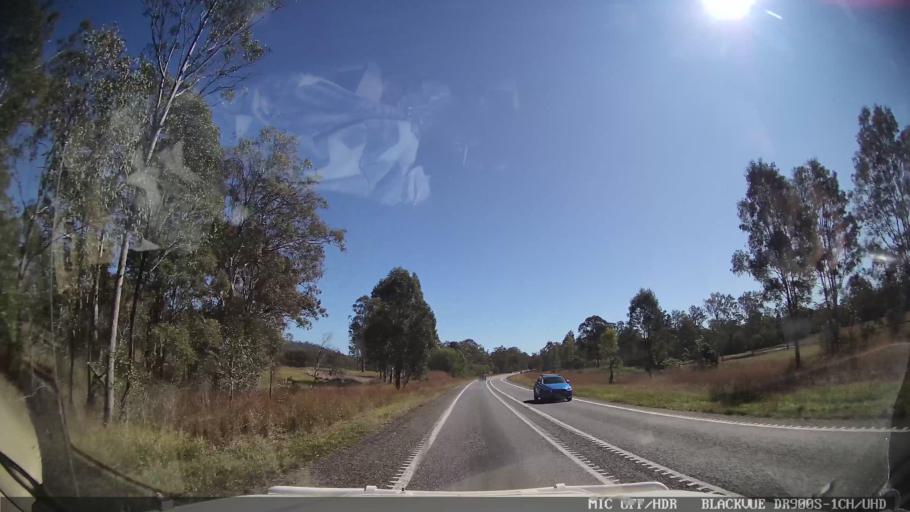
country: AU
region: Queensland
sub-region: Gympie Regional Council
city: Gympie
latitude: -26.0455
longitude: 152.5735
